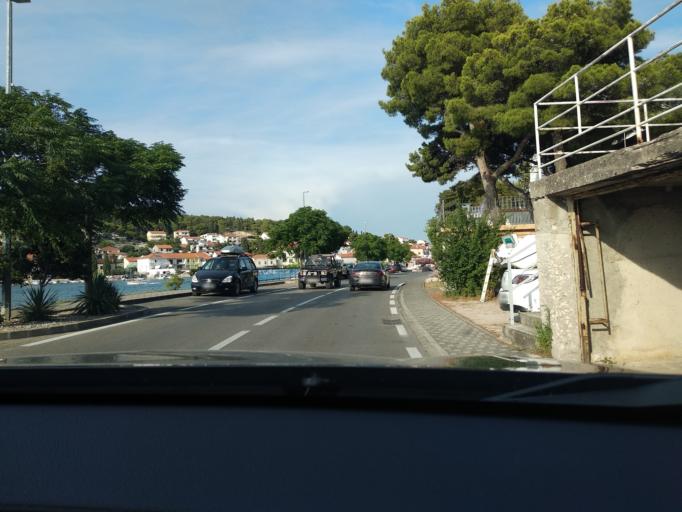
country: HR
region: Sibensko-Kniniska
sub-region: Grad Sibenik
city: Tisno
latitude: 43.7990
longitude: 15.6377
